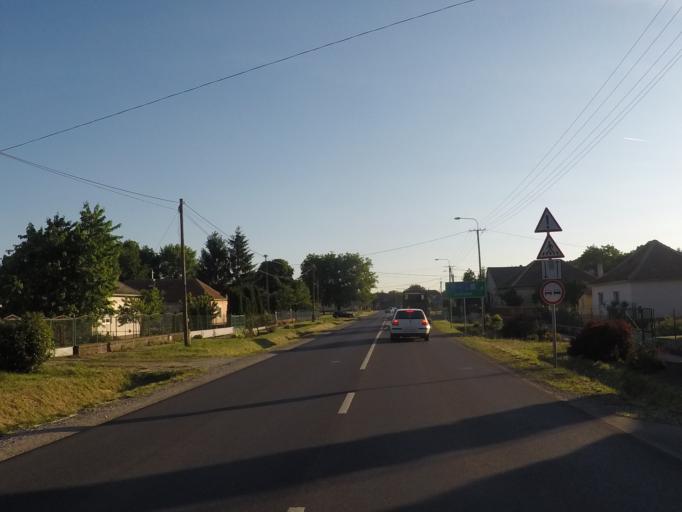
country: HU
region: Heves
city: Erdotelek
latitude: 47.6577
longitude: 20.3454
